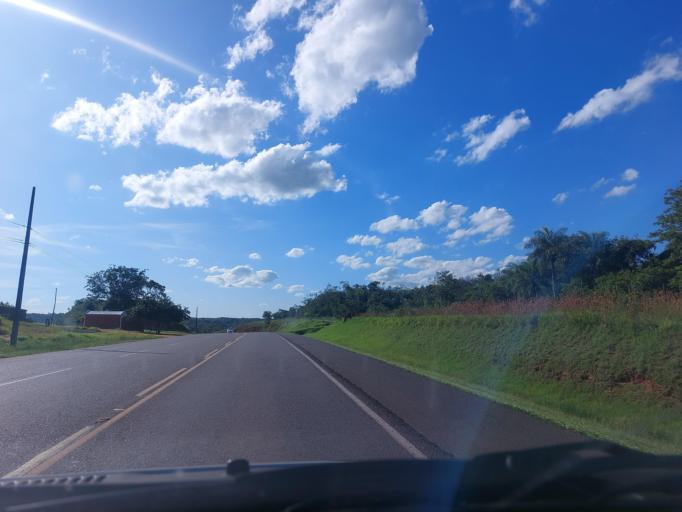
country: PY
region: San Pedro
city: Guayaybi
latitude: -24.6111
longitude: -56.4827
